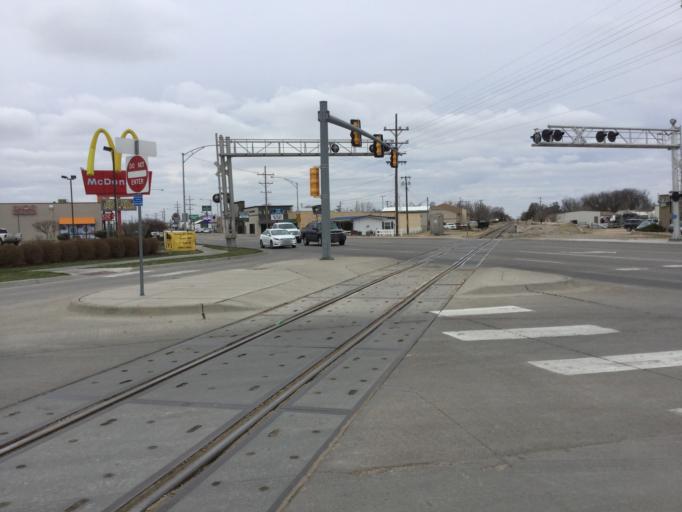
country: US
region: Kansas
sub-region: Barton County
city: Great Bend
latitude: 38.3616
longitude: -98.7836
